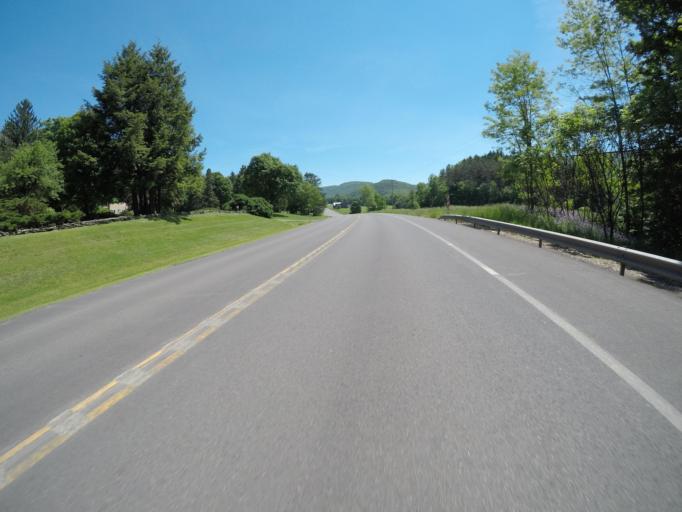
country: US
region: New York
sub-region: Delaware County
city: Walton
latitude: 42.1683
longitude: -75.0378
